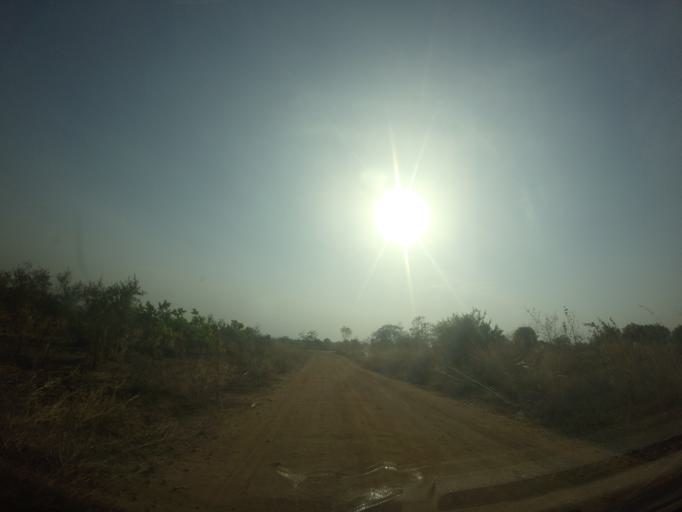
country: UG
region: Northern Region
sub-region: Maracha District
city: Maracha
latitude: 3.1120
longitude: 31.1562
